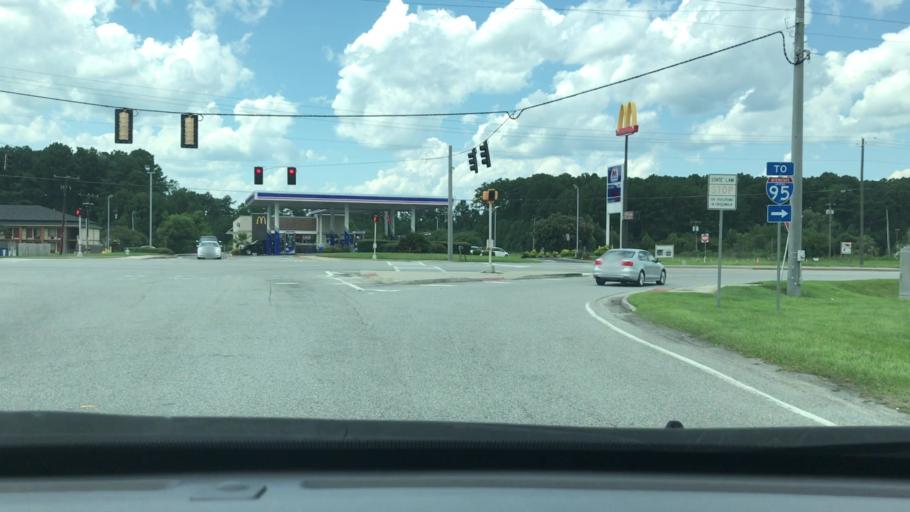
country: US
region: Georgia
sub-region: Bryan County
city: Richmond Hill
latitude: 31.9252
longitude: -81.3338
